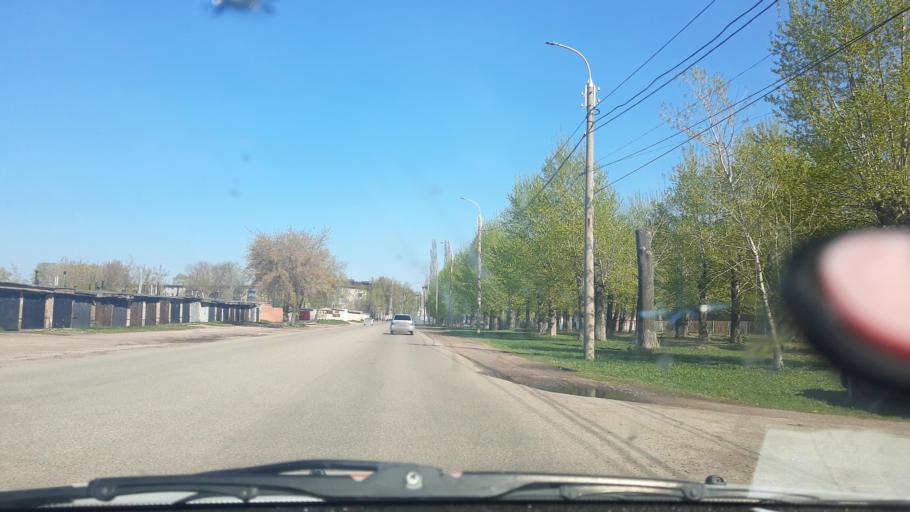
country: RU
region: Bashkortostan
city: Sterlitamak
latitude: 53.6384
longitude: 55.9211
